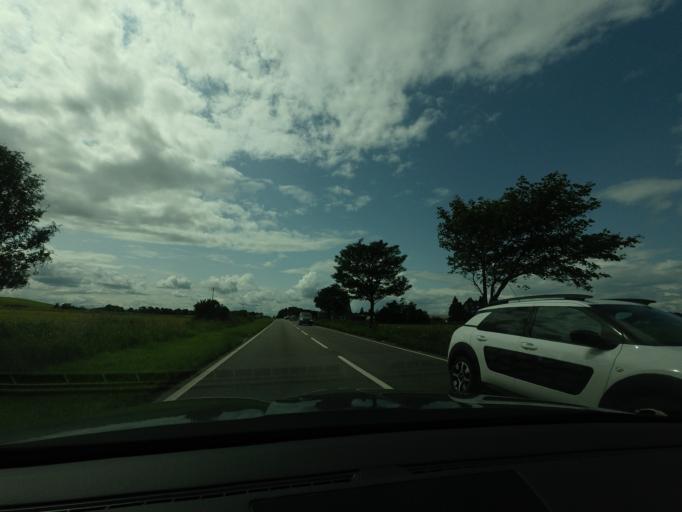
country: GB
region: Scotland
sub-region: Moray
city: Kinloss
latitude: 57.6253
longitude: -3.5264
